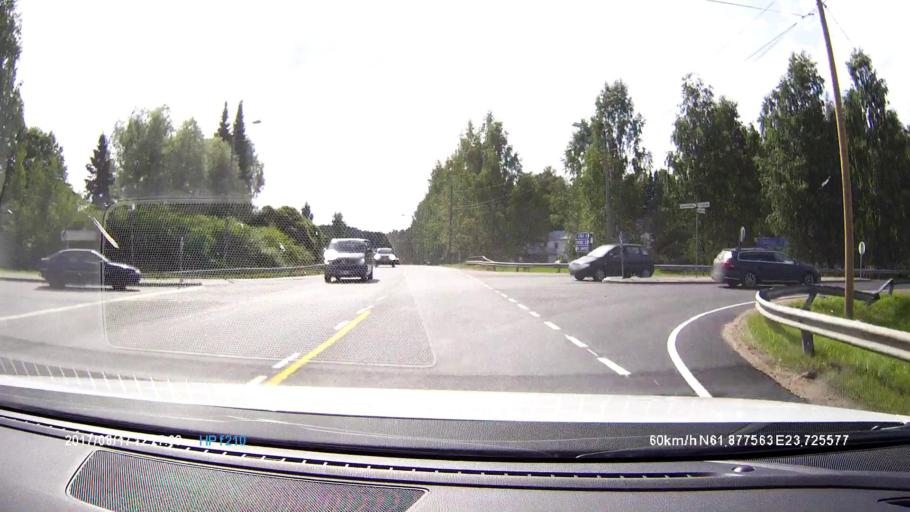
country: FI
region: Pirkanmaa
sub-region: Tampere
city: Kuru
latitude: 61.8772
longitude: 23.7255
